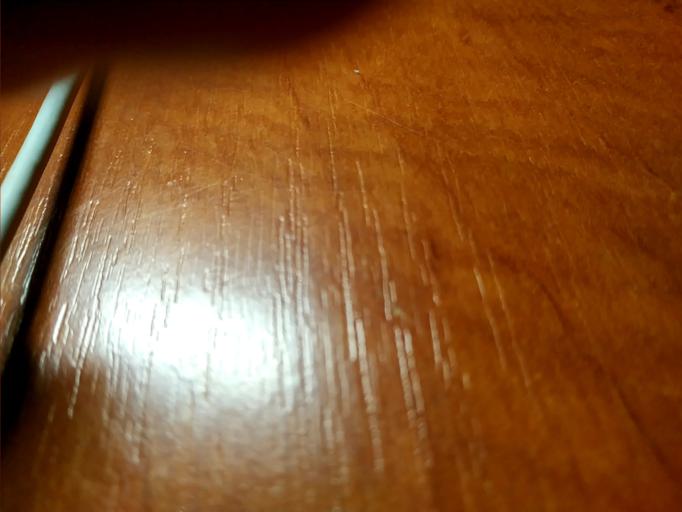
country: RU
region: Orjol
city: Naryshkino
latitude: 52.9750
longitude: 35.7067
